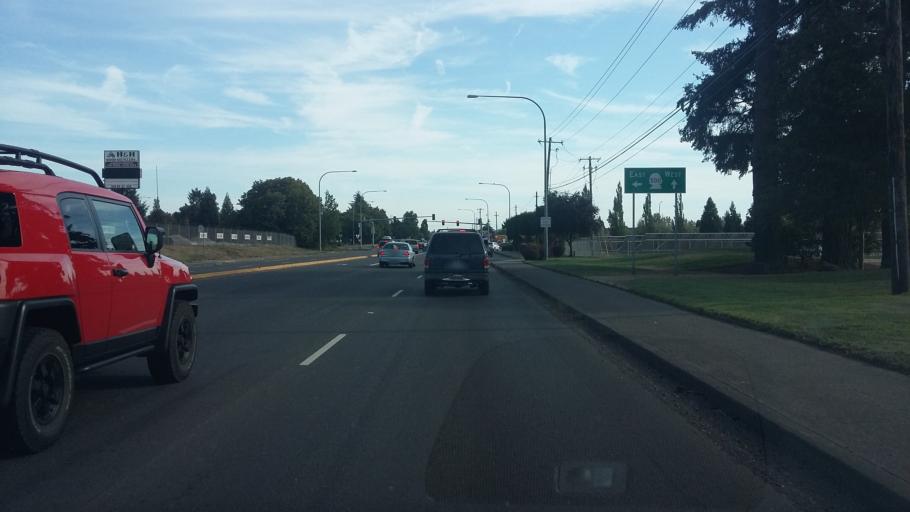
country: US
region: Washington
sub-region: Clark County
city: Orchards
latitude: 45.6839
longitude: -122.5527
